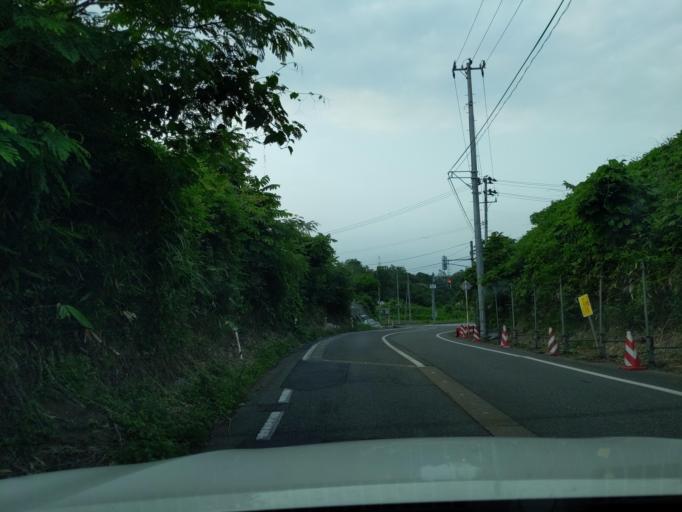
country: JP
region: Niigata
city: Kashiwazaki
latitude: 37.3972
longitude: 138.5957
